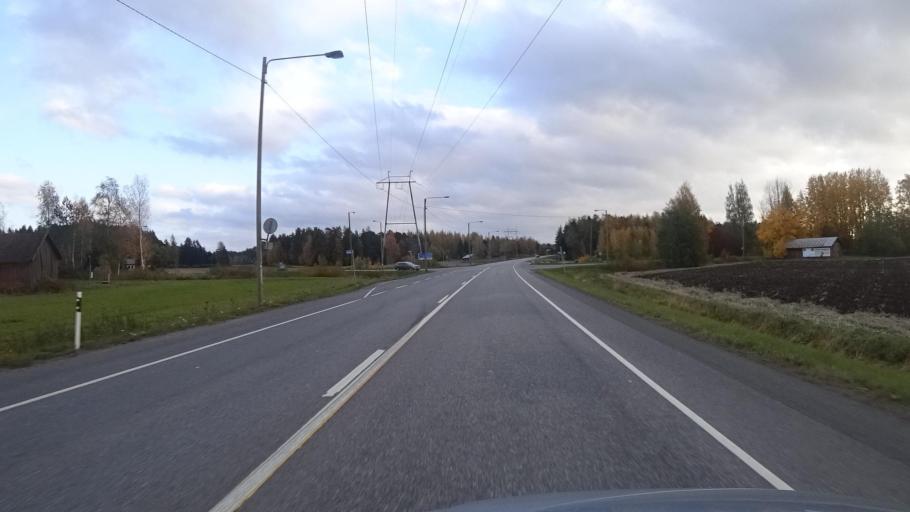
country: FI
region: Satakunta
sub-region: Rauma
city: Saekylae
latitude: 61.0222
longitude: 22.4078
